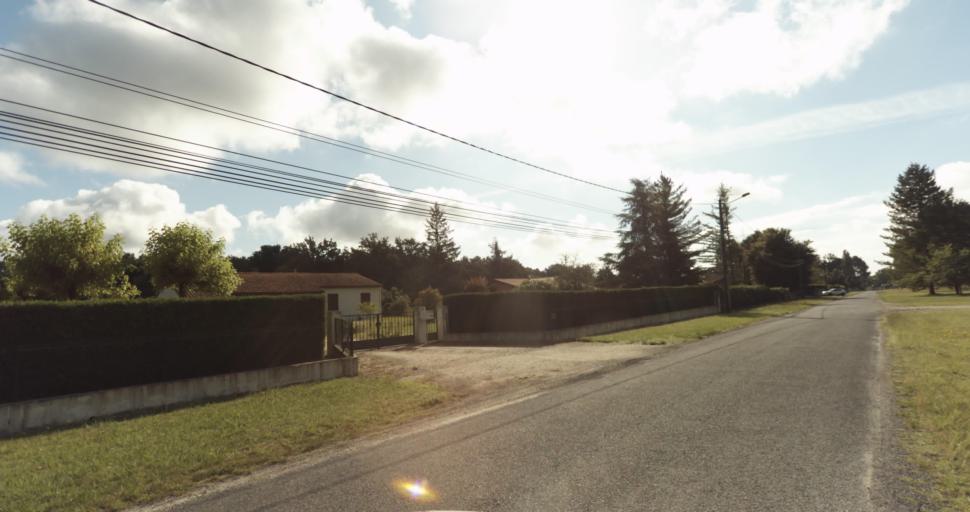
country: FR
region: Aquitaine
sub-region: Departement de la Gironde
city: Bazas
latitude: 44.4366
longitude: -0.2496
